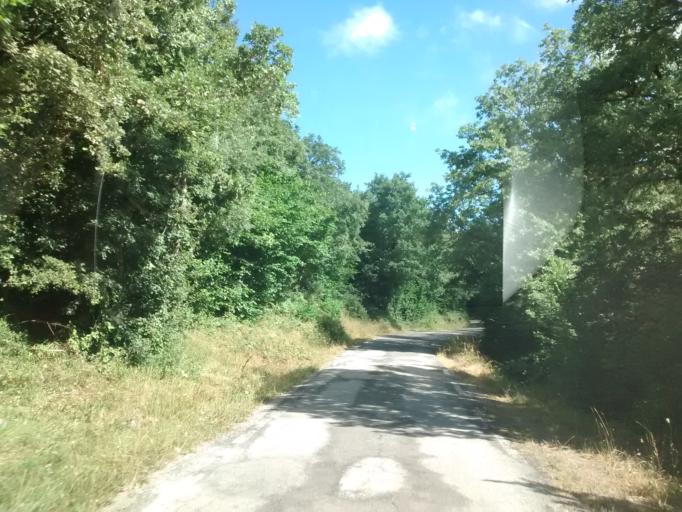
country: ES
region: Castille and Leon
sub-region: Provincia de Palencia
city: Berzosilla
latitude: 42.8767
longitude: -4.0530
